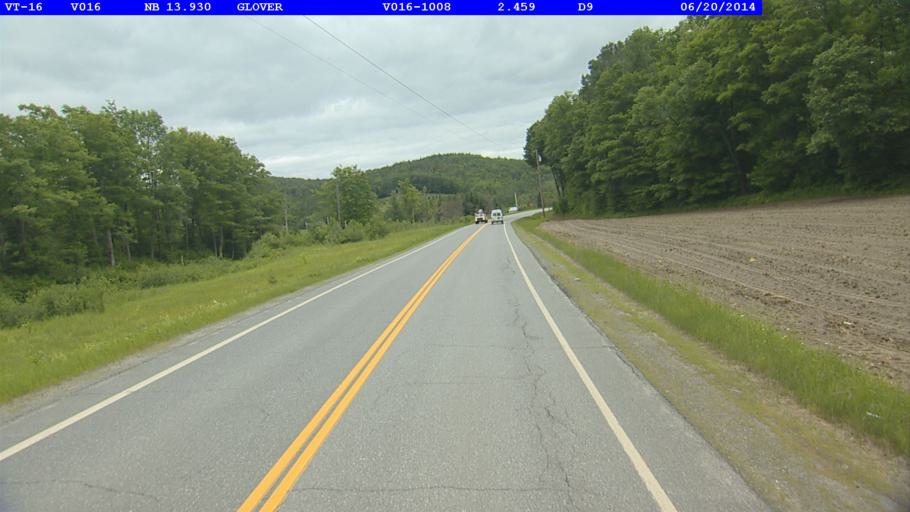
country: US
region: Vermont
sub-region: Caledonia County
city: Hardwick
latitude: 44.6593
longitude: -72.1984
